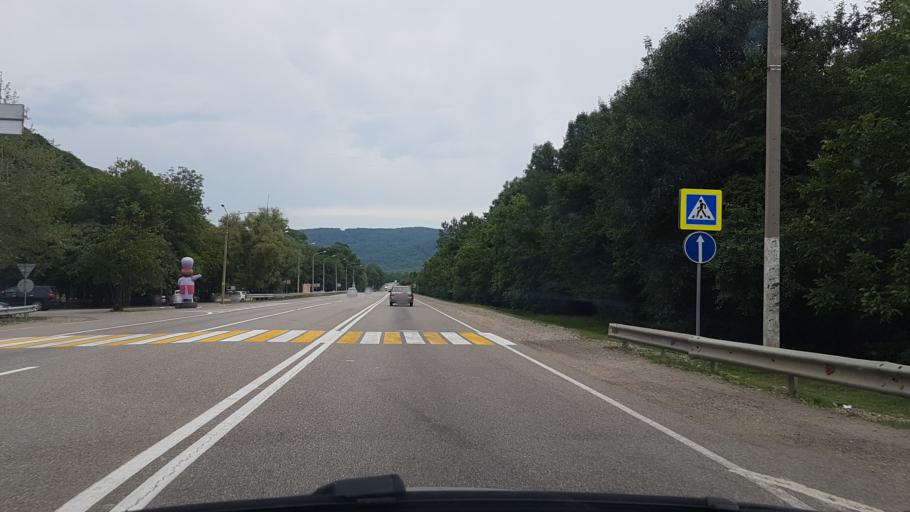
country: RU
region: Krasnodarskiy
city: Goryachiy Klyuch
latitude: 44.6228
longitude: 39.0901
